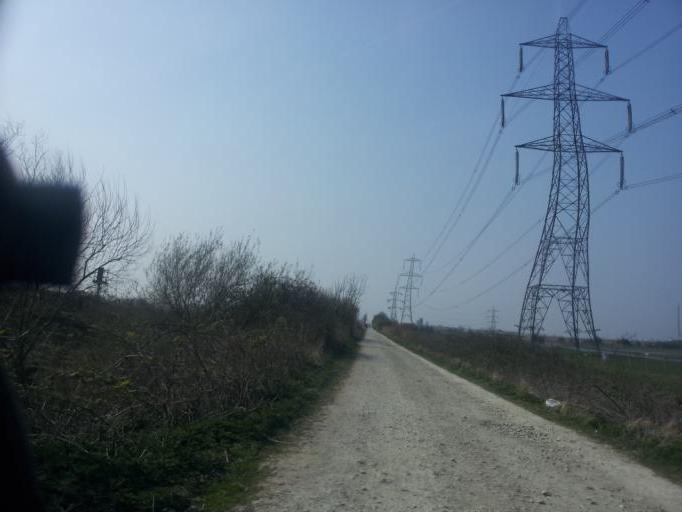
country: GB
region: England
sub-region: Kent
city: Gravesend
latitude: 51.4383
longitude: 0.4232
